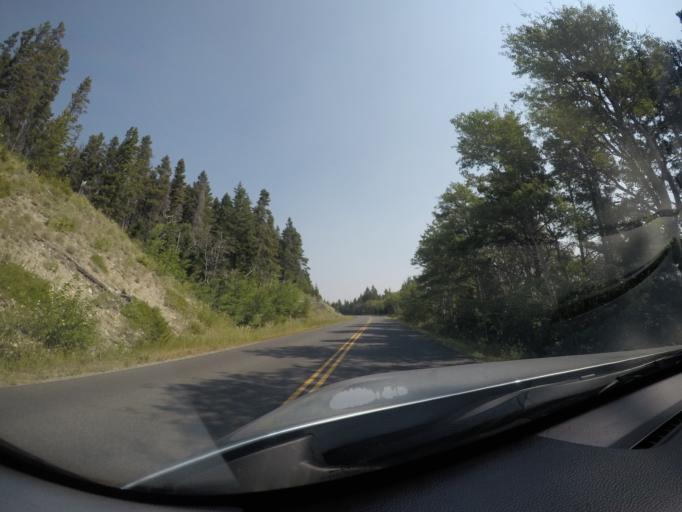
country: US
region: Montana
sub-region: Glacier County
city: North Browning
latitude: 48.7055
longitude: -113.4963
